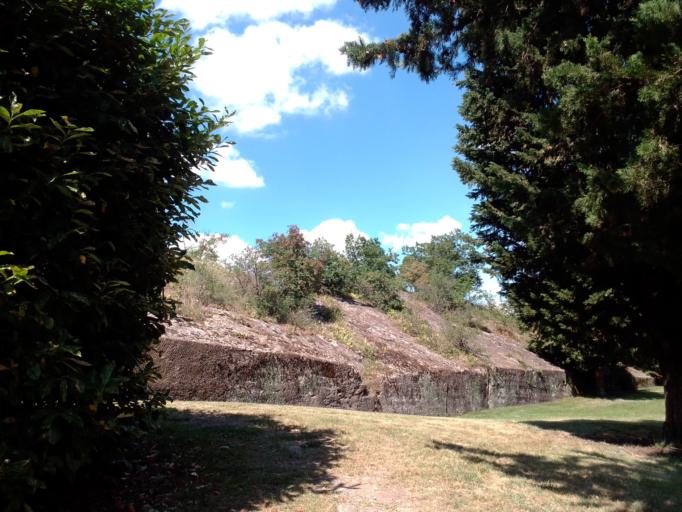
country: IT
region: Emilia-Romagna
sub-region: Provincia di Piacenza
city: Pianello Val Tidone
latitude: 44.9145
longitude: 9.3941
